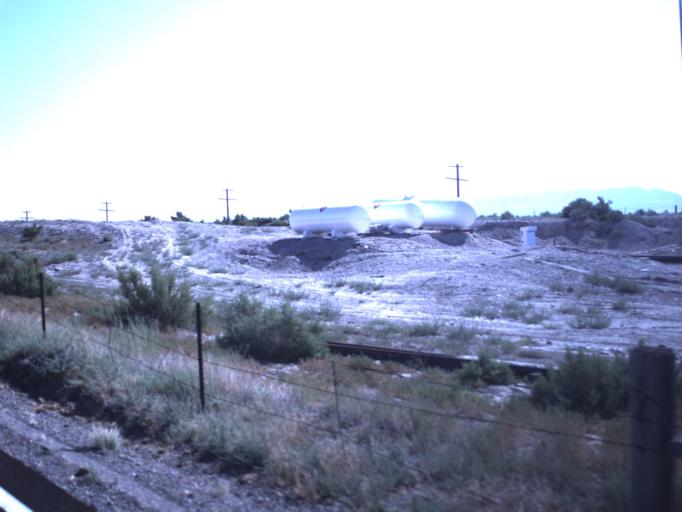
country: US
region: Utah
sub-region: Millard County
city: Delta
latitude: 39.2263
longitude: -112.6716
